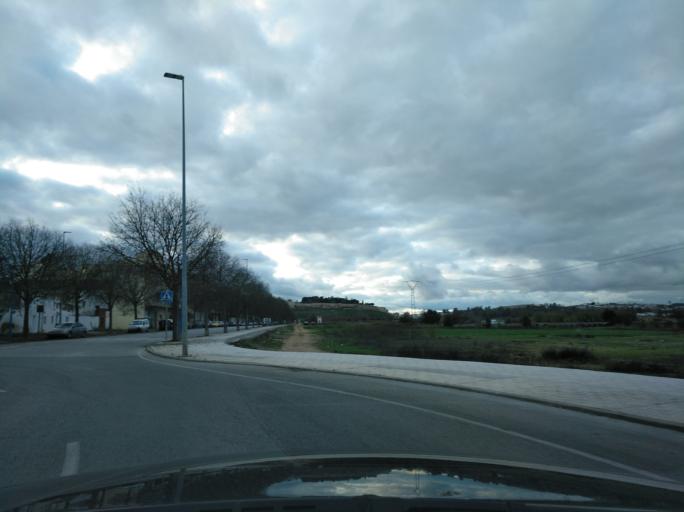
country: ES
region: Extremadura
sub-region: Provincia de Badajoz
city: Badajoz
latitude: 38.8828
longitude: -6.9552
